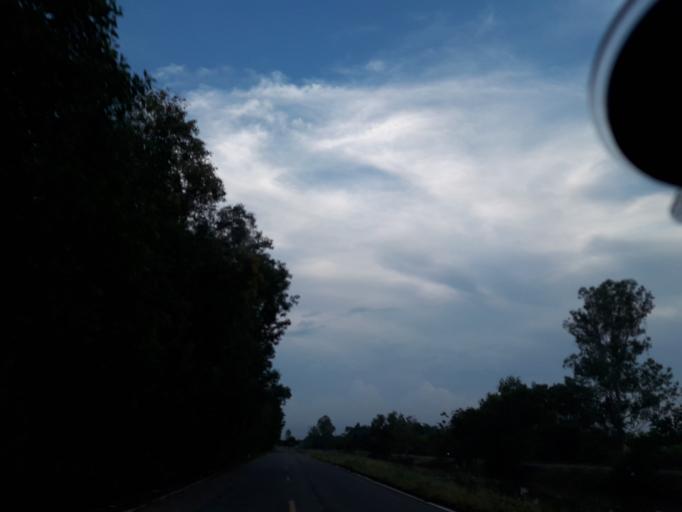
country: TH
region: Pathum Thani
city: Nong Suea
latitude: 14.2153
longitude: 100.8689
